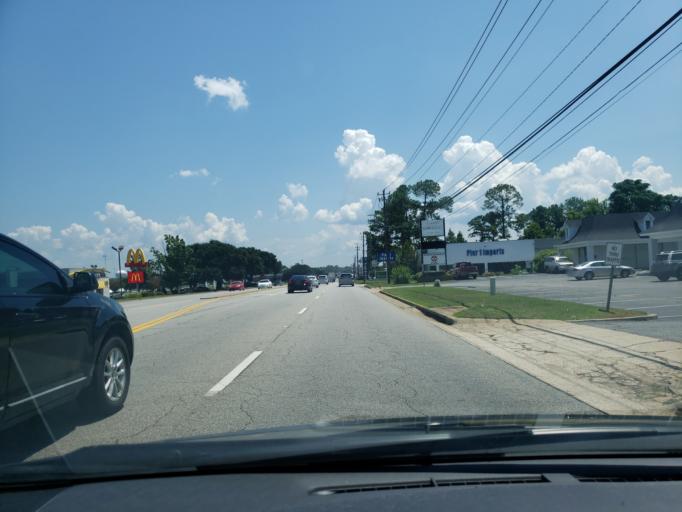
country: US
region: Georgia
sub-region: Dougherty County
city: Albany
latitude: 31.6169
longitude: -84.2210
